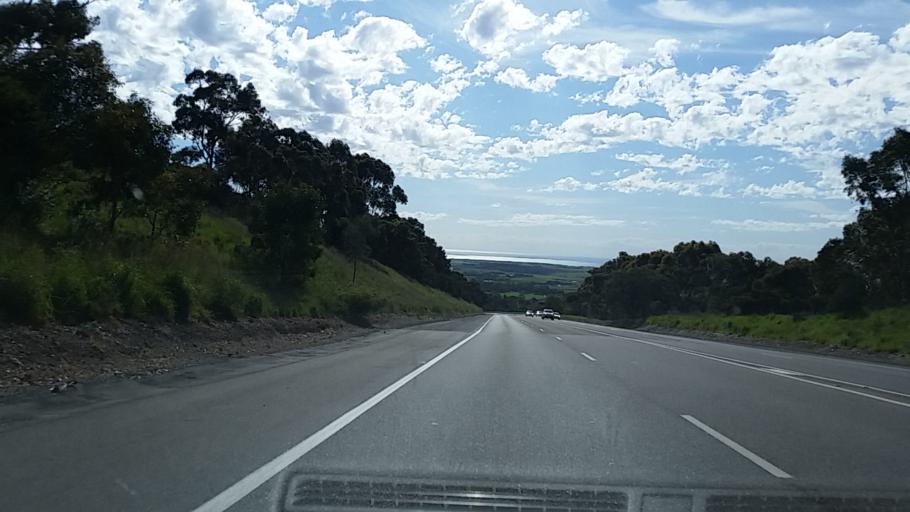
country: AU
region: South Australia
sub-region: Onkaparinga
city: McLaren Vale
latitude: -35.2811
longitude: 138.5616
